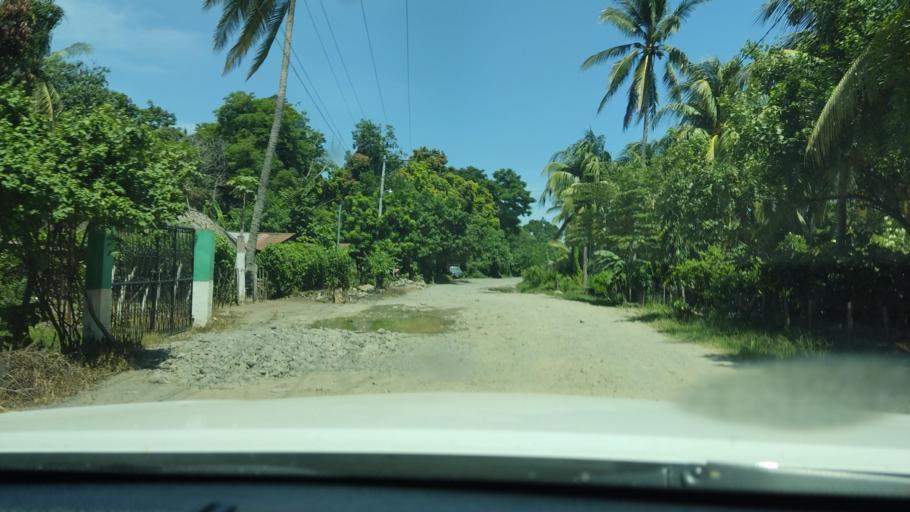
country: SV
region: Ahuachapan
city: San Francisco Menendez
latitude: 13.7777
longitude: -90.1140
